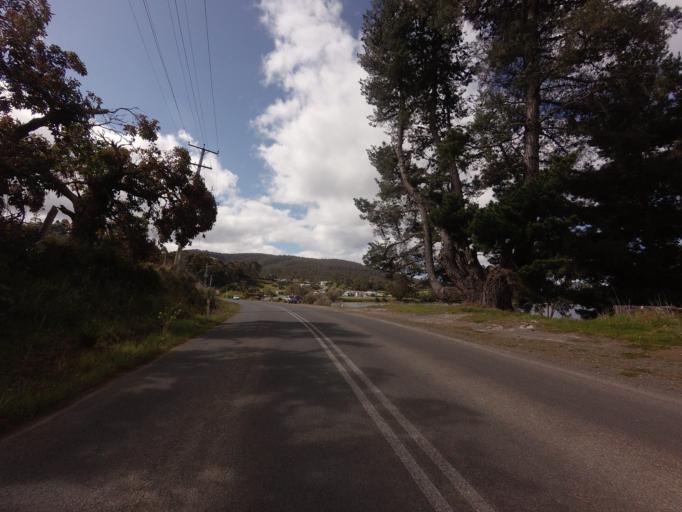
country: AU
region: Tasmania
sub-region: Huon Valley
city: Cygnet
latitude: -43.3178
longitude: 147.0104
